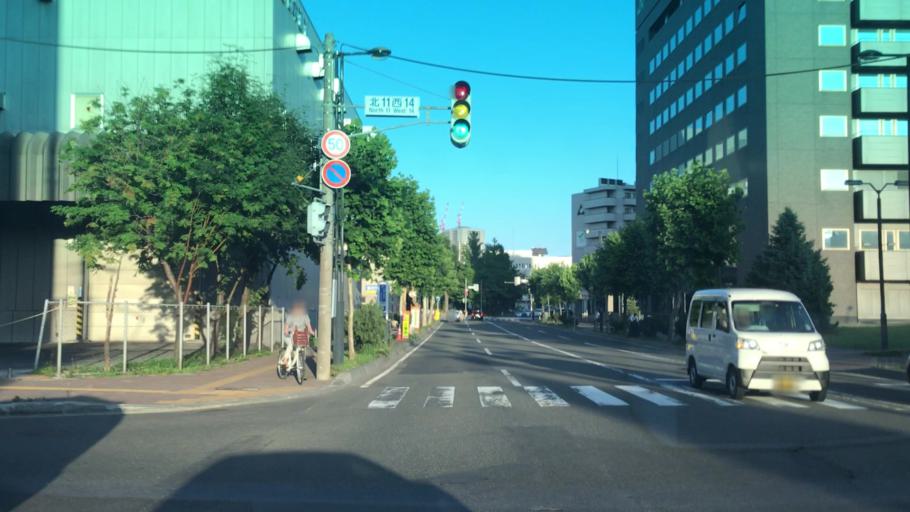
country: JP
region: Hokkaido
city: Sapporo
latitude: 43.0717
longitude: 141.3315
